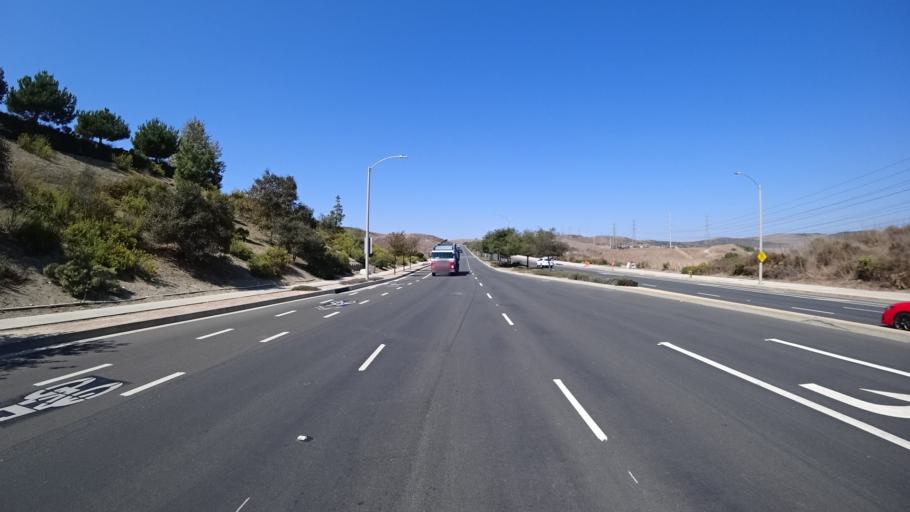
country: US
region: California
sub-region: Orange County
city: San Clemente
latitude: 33.4646
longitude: -117.6053
